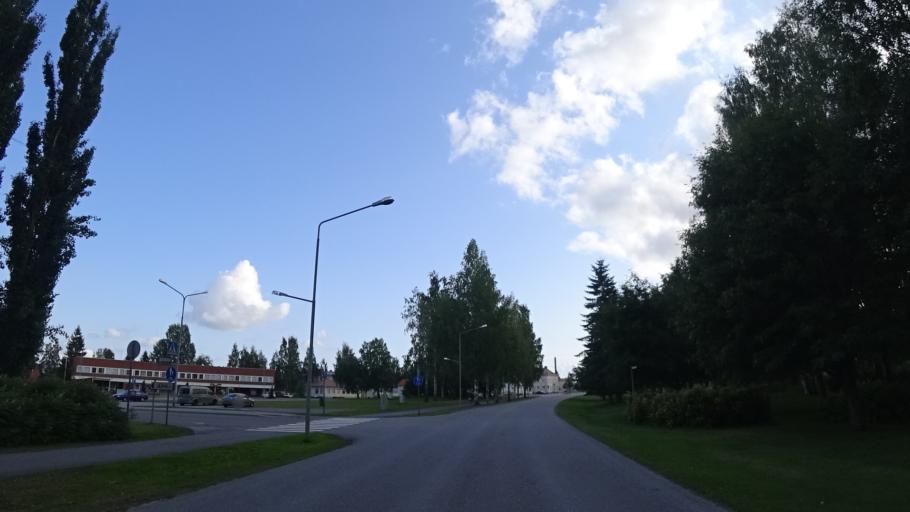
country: FI
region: North Karelia
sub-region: Pielisen Karjala
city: Lieksa
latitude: 63.3218
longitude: 30.0225
